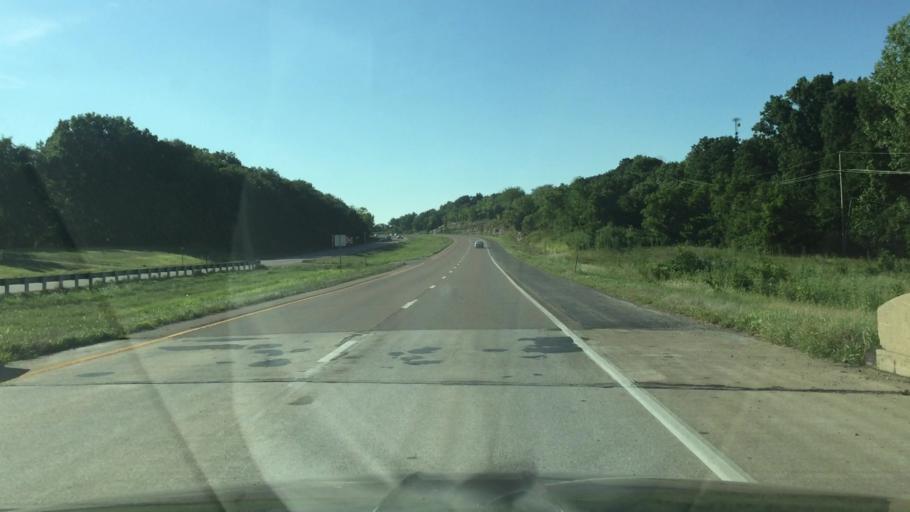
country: US
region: Missouri
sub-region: Pettis County
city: Sedalia
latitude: 38.7290
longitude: -93.3054
